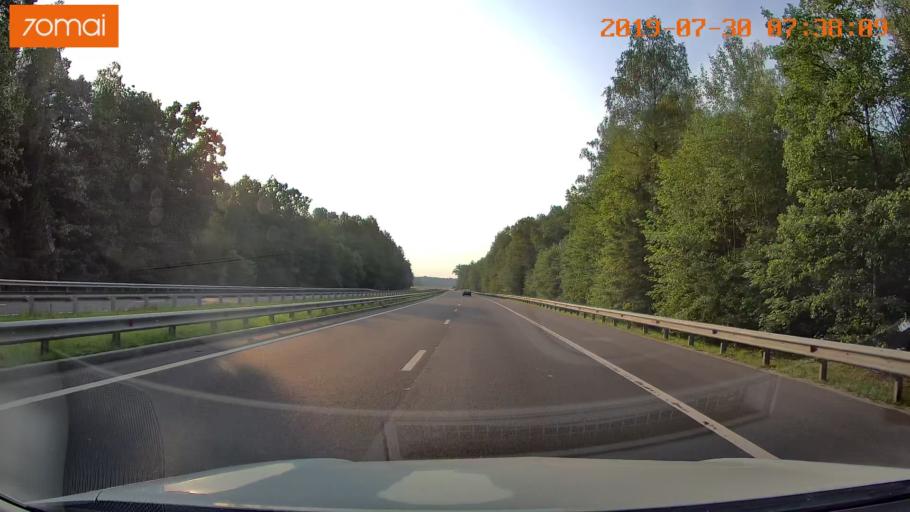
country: RU
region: Kaliningrad
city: Gvardeysk
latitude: 54.6512
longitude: 21.1609
